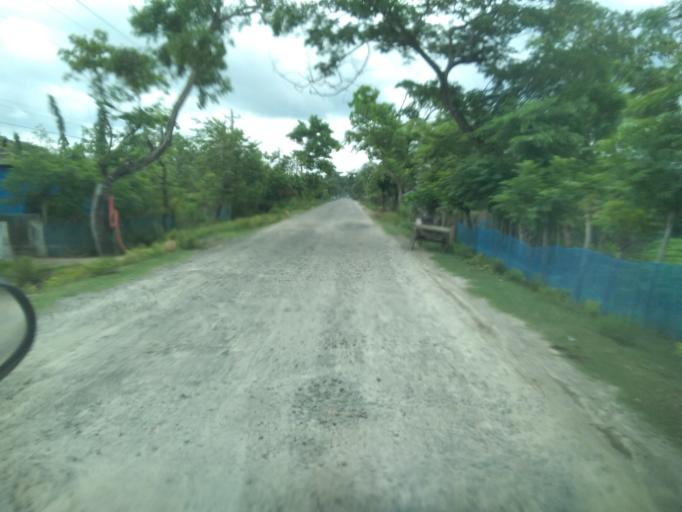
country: IN
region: West Bengal
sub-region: North 24 Parganas
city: Gosaba
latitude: 22.2696
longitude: 89.1605
